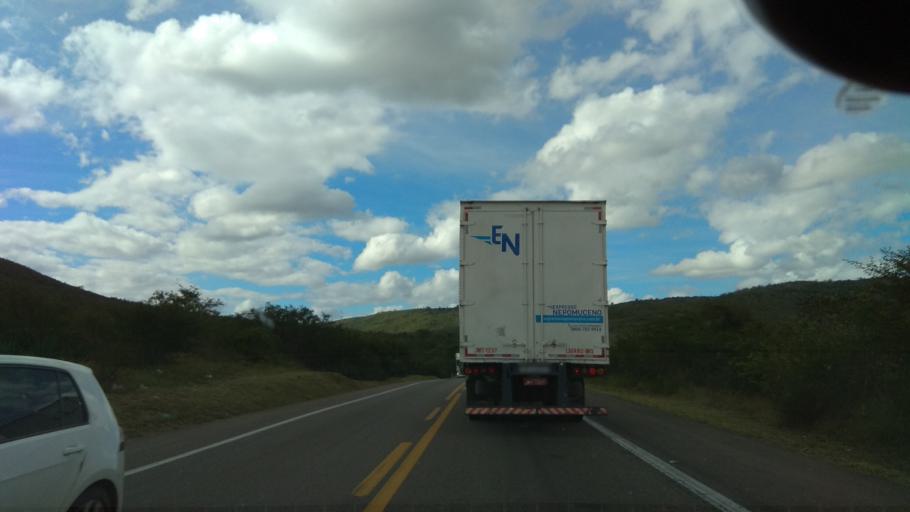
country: BR
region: Bahia
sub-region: Amargosa
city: Amargosa
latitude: -12.9168
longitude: -39.8708
